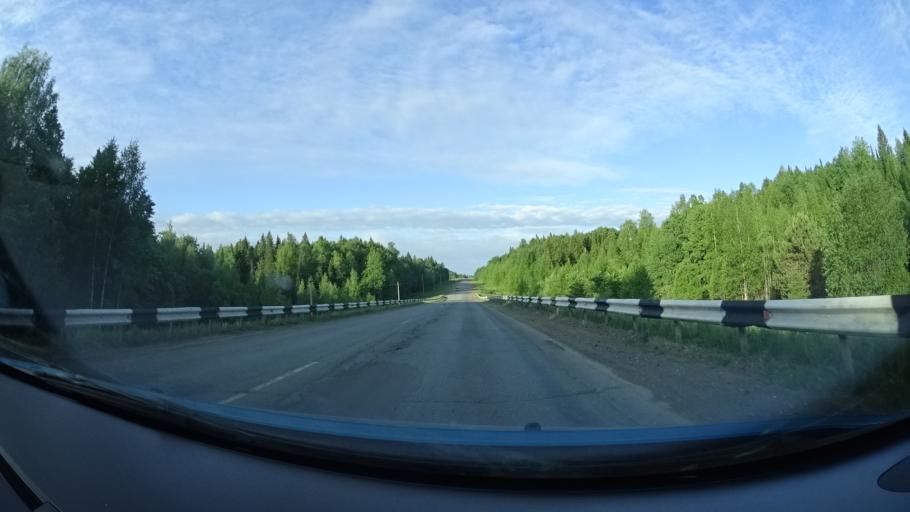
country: RU
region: Perm
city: Kultayevo
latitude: 57.8318
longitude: 55.8152
